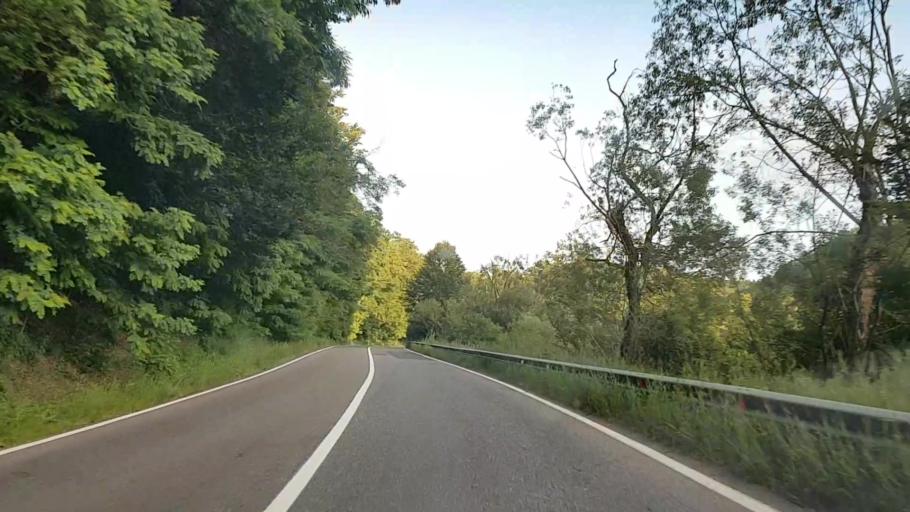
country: RO
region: Harghita
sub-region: Comuna Corund
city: Corund
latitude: 46.4540
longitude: 25.2112
